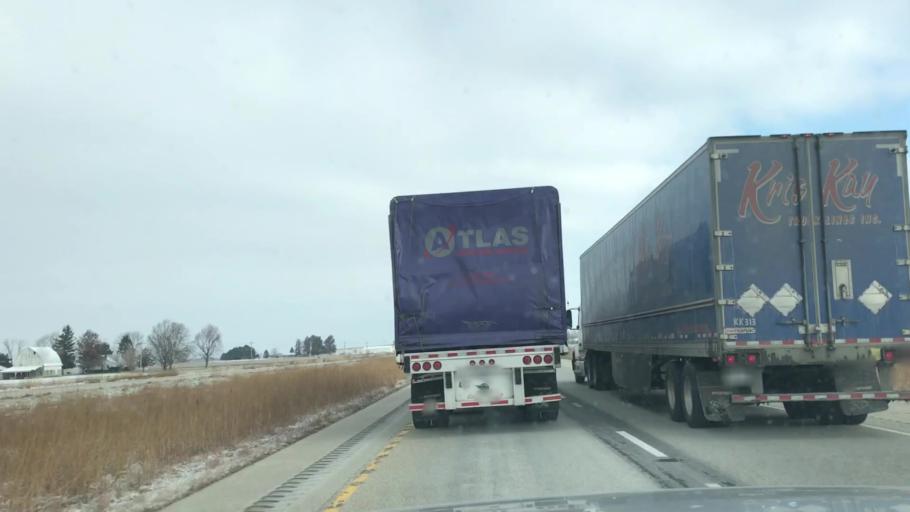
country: US
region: Illinois
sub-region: Sangamon County
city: Divernon
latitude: 39.5166
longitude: -89.6453
